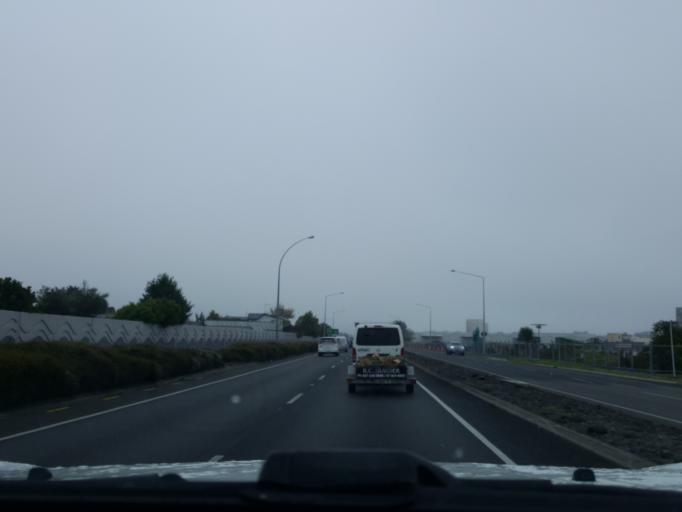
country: NZ
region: Waikato
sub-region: Hamilton City
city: Hamilton
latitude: -37.7683
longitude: 175.2381
